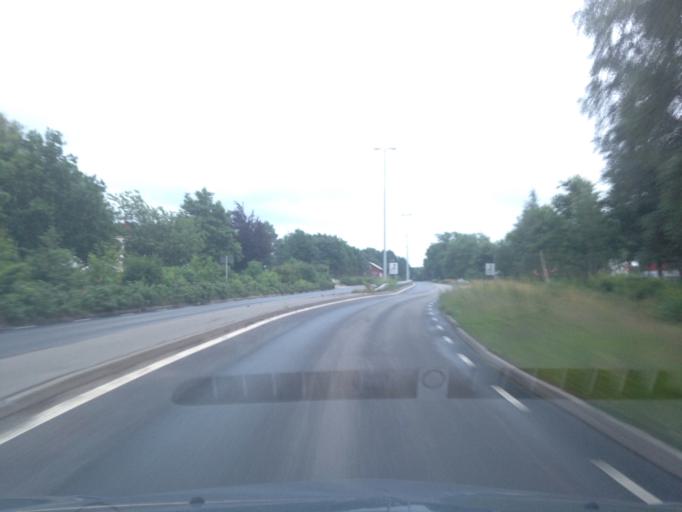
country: SE
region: Halland
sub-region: Varbergs Kommun
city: Varberg
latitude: 57.1161
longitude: 12.2607
